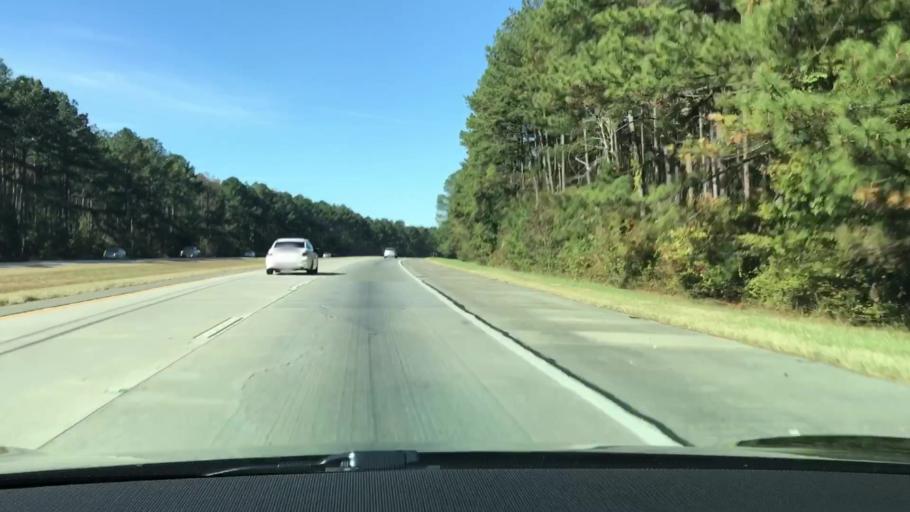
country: US
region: Georgia
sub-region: Taliaferro County
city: Crawfordville
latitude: 33.5316
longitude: -82.9837
